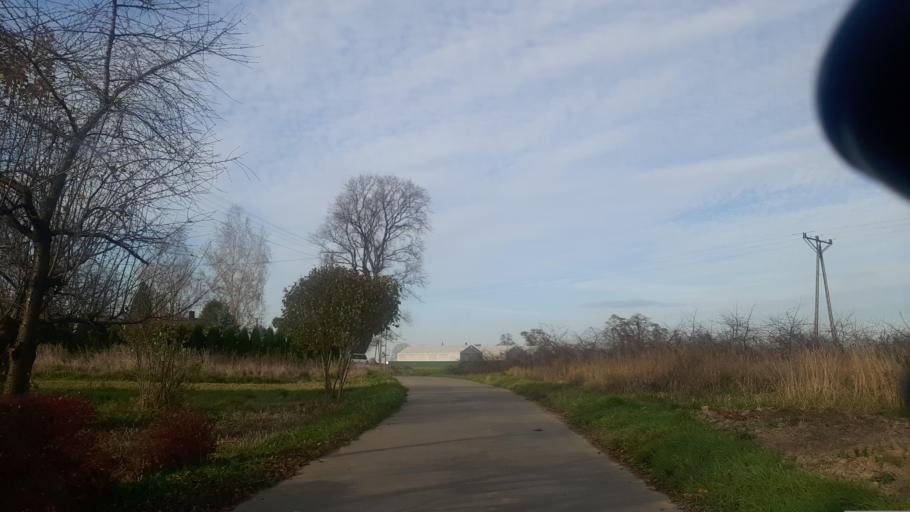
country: PL
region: Lublin Voivodeship
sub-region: Powiat pulawski
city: Markuszow
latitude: 51.3679
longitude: 22.2724
